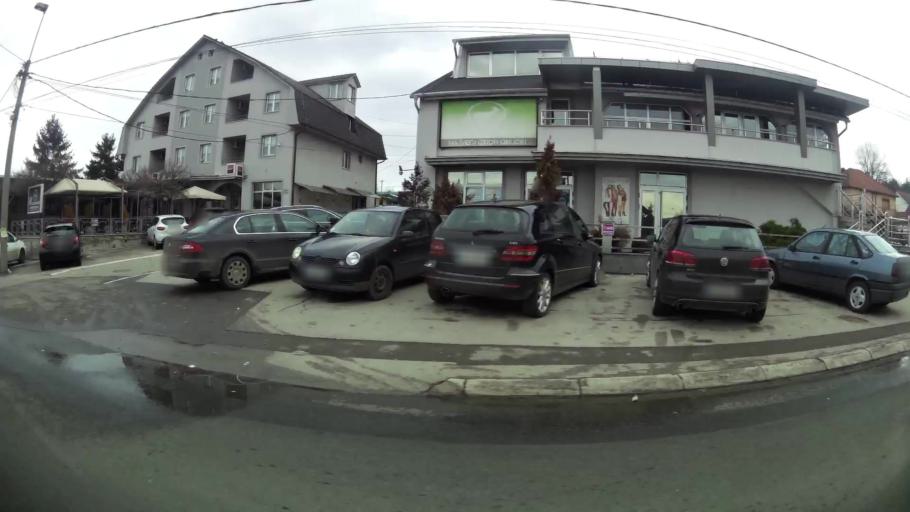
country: RS
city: Ostruznica
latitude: 44.7279
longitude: 20.3674
